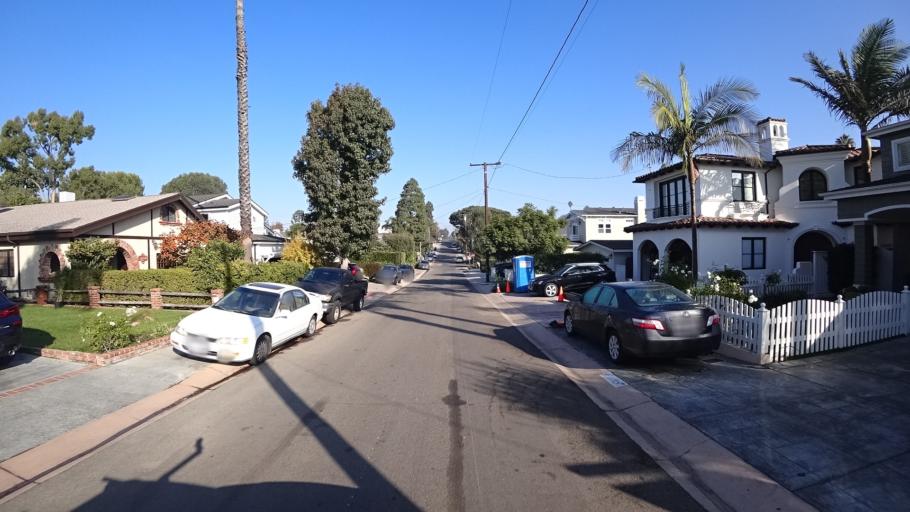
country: US
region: California
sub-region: Los Angeles County
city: Manhattan Beach
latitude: 33.8916
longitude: -118.3978
